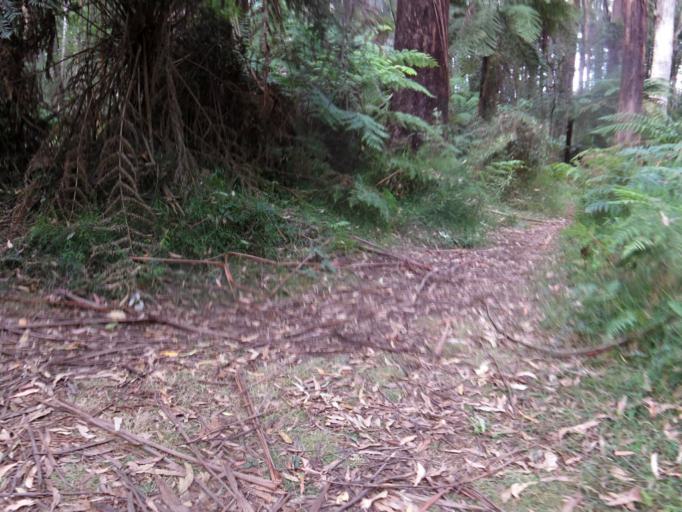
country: AU
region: Victoria
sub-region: Yarra Ranges
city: Healesville
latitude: -37.5396
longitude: 145.4817
